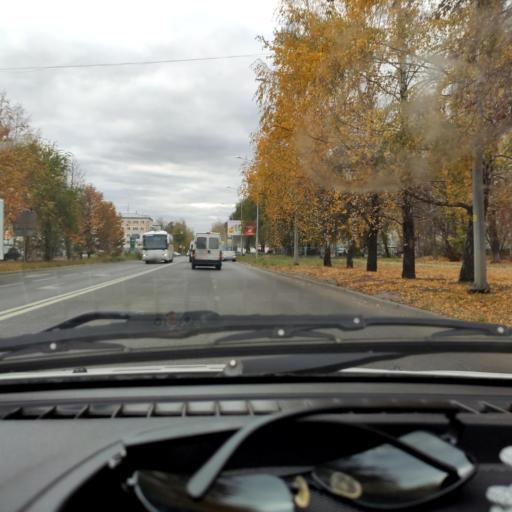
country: RU
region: Samara
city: Tol'yatti
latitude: 53.5395
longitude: 49.4092
